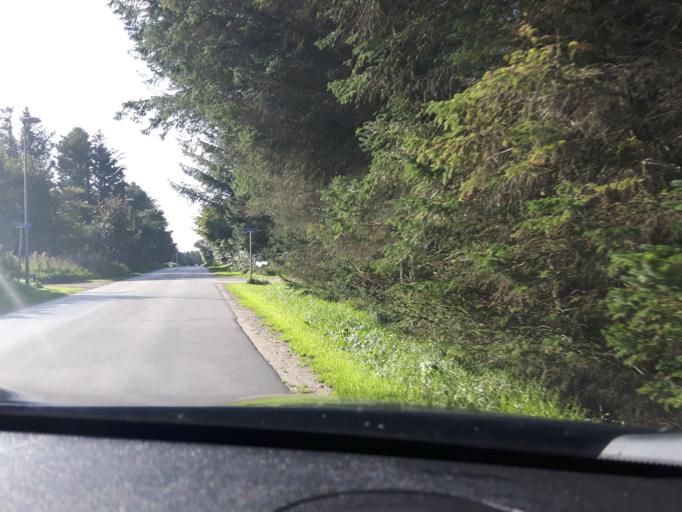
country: DK
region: North Denmark
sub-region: Hjorring Kommune
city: Hjorring
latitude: 57.4718
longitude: 9.8079
